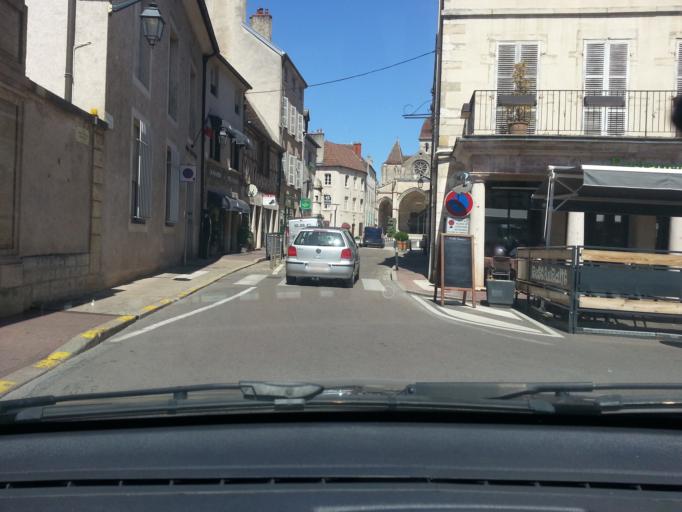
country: FR
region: Bourgogne
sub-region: Departement de la Cote-d'Or
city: Beaune
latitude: 47.0232
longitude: 4.8351
